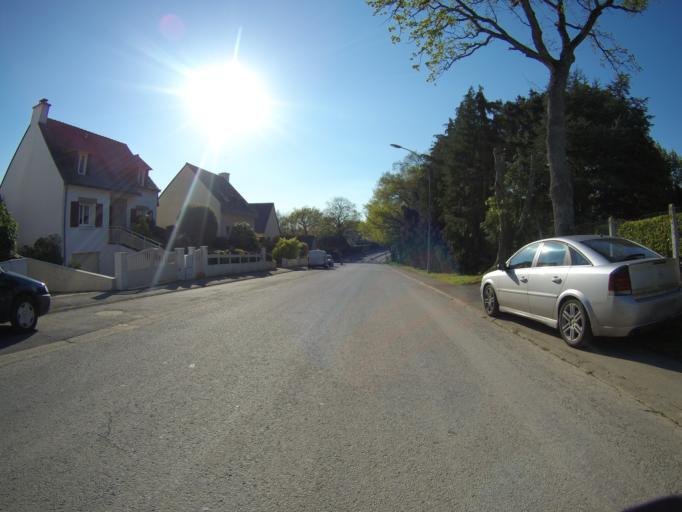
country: FR
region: Brittany
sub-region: Departement d'Ille-et-Vilaine
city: Vern-sur-Seiche
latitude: 48.0416
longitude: -1.5932
